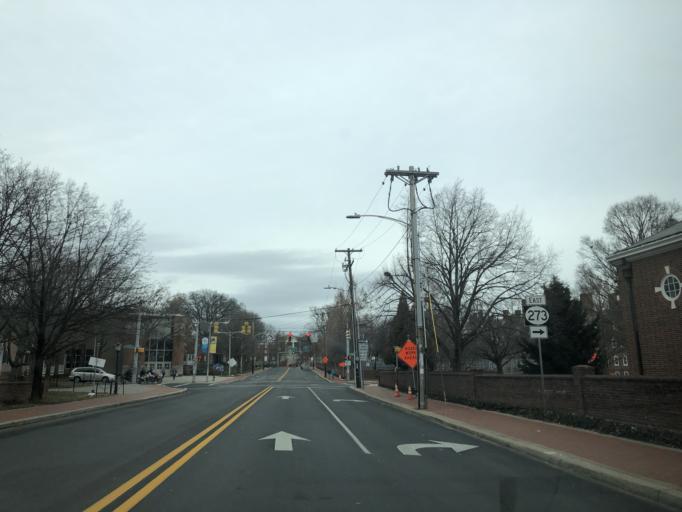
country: US
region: Delaware
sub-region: New Castle County
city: Newark
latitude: 39.6810
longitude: -75.7536
